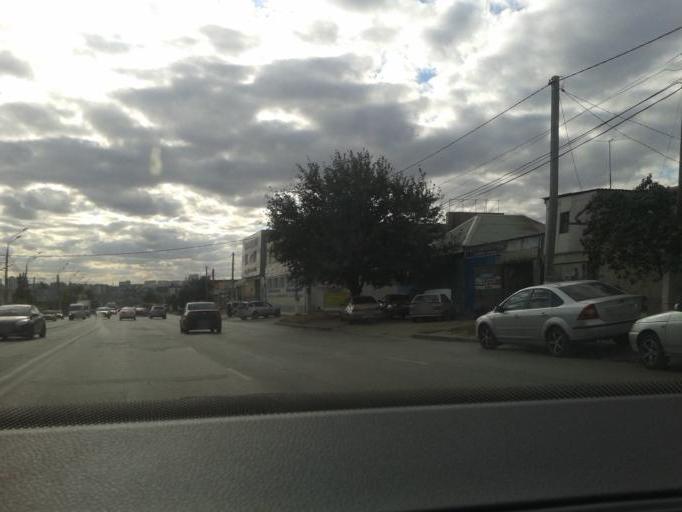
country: RU
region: Volgograd
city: Volgograd
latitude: 48.6944
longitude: 44.4656
